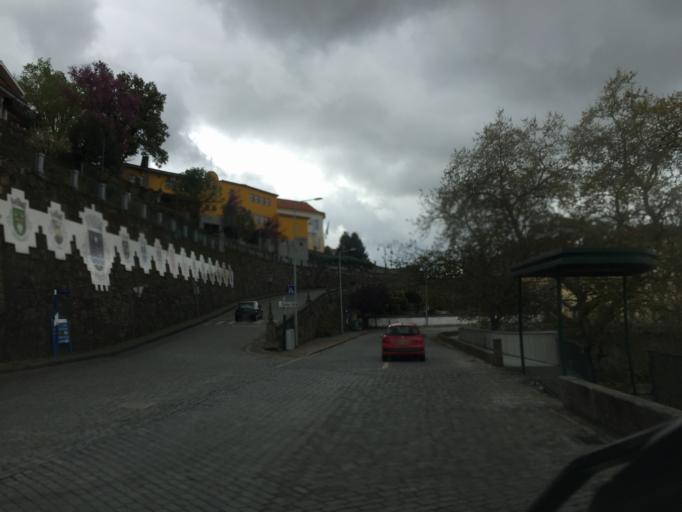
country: PT
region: Guarda
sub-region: Manteigas
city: Manteigas
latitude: 40.4928
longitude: -7.5943
